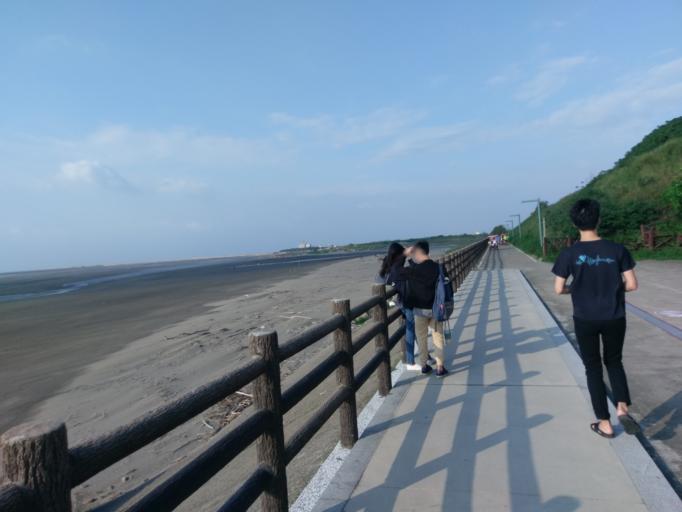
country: TW
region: Taiwan
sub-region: Hsinchu
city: Hsinchu
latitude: 24.8356
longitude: 120.9166
